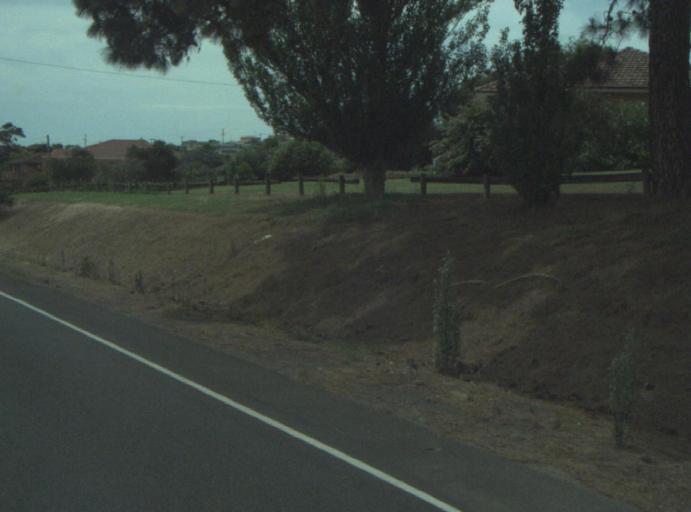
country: AU
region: Victoria
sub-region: Greater Geelong
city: Clifton Springs
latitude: -38.1174
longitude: 144.6408
